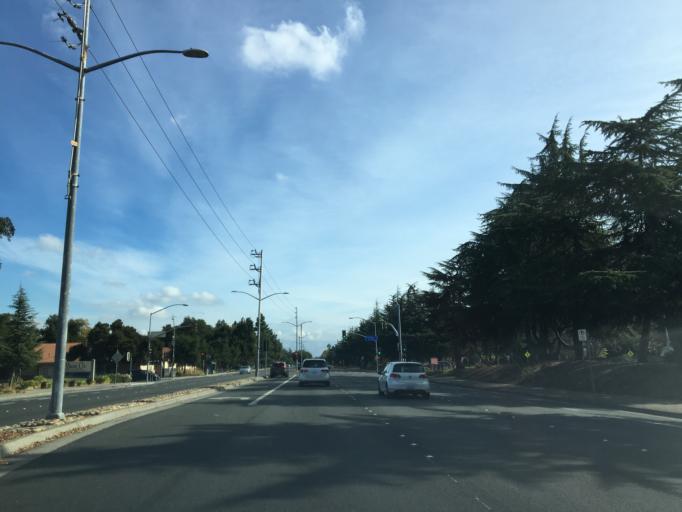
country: US
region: California
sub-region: Santa Clara County
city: Cupertino
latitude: 37.3228
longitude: -122.0473
